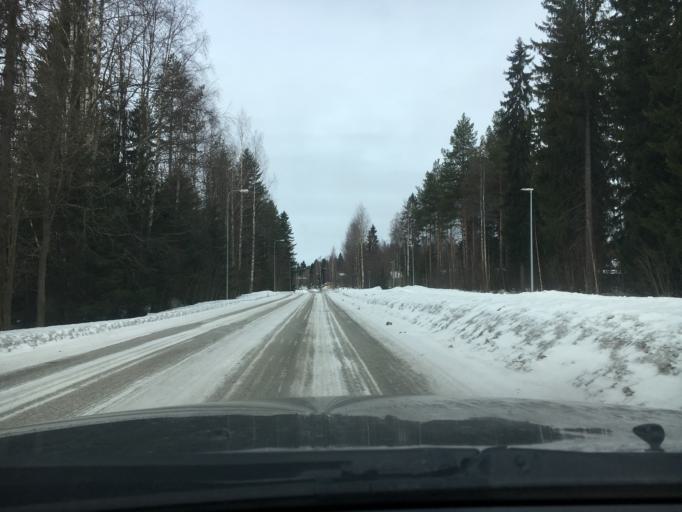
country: FI
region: Kainuu
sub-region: Kajaani
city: Kajaani
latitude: 64.2302
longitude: 27.7506
